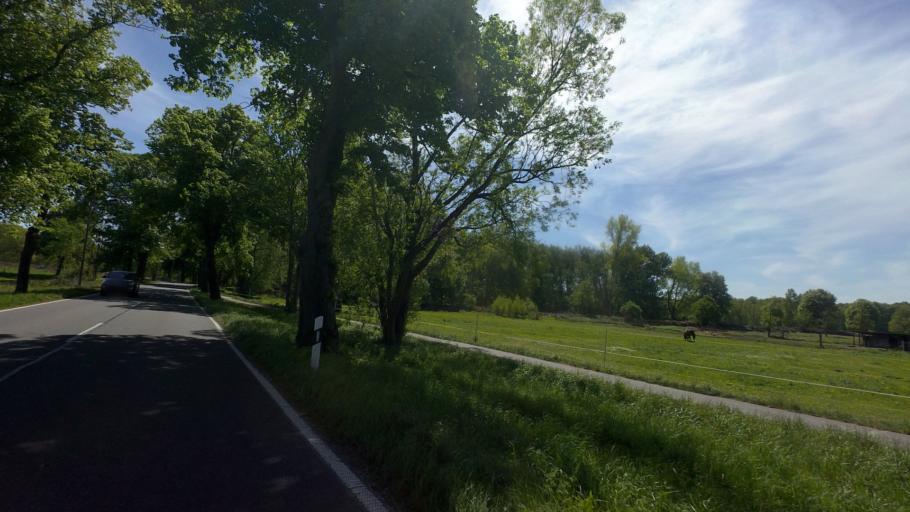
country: DE
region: Brandenburg
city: Luckenwalde
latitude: 52.0759
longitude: 13.1851
